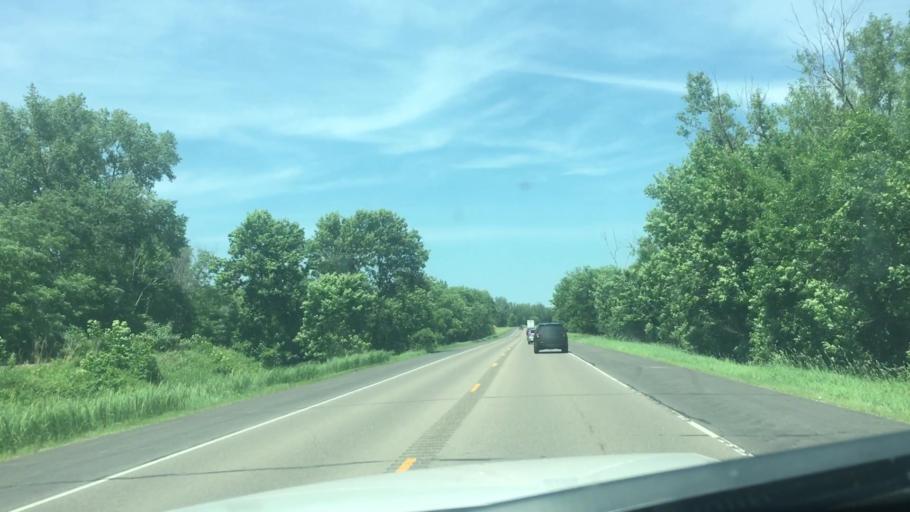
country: US
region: Minnesota
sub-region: Ramsey County
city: White Bear Lake
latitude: 45.1133
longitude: -93.0006
